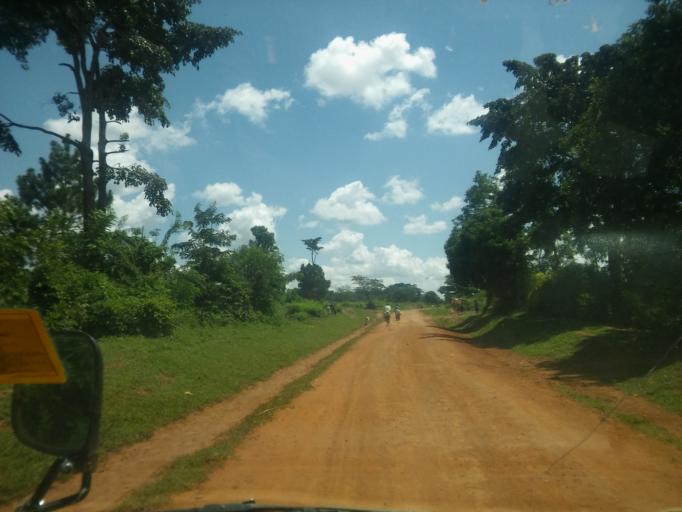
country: UG
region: Eastern Region
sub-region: Budaka District
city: Budaka
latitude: 1.1130
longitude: 33.9526
